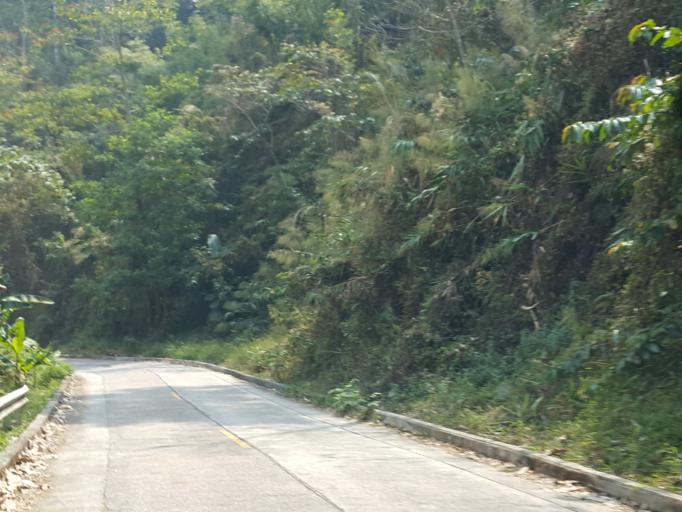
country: TH
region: Chiang Mai
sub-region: Amphoe Chiang Dao
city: Chiang Dao
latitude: 19.4114
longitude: 98.8580
